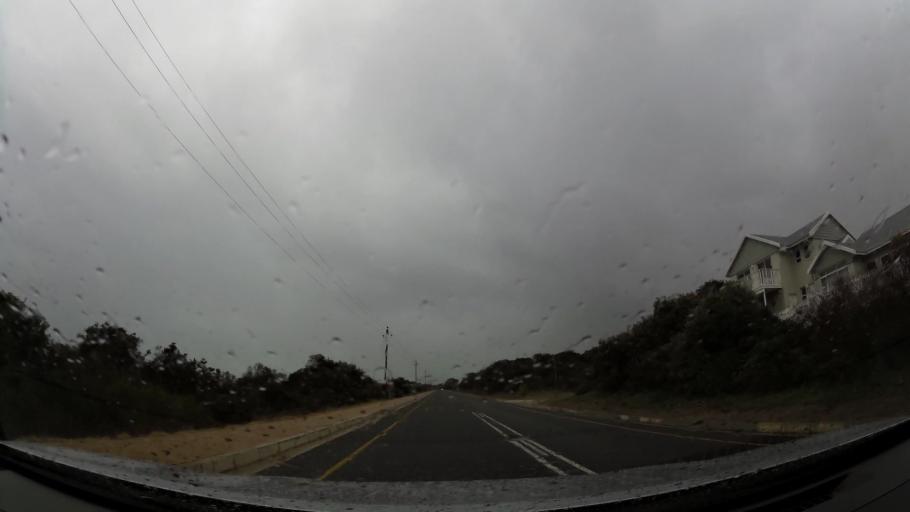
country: ZA
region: Western Cape
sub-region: Eden District Municipality
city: Mossel Bay
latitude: -34.0492
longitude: 22.2781
